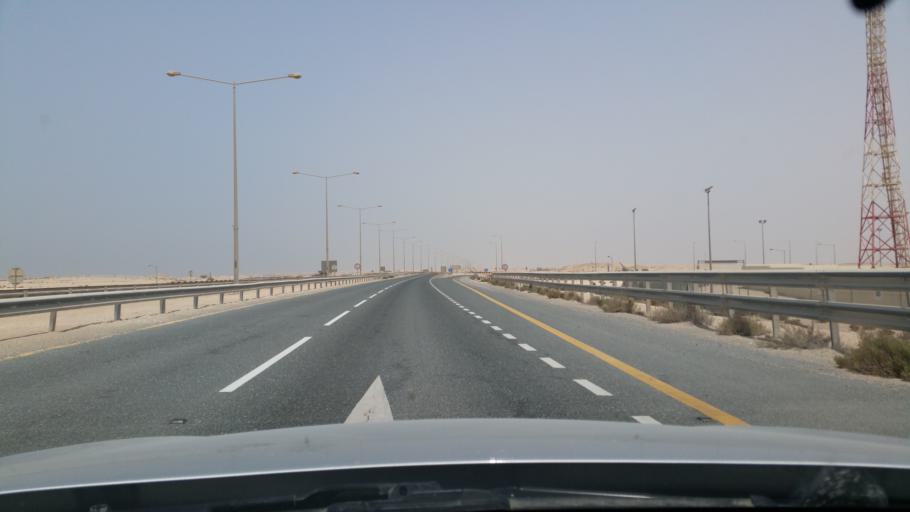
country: QA
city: Umm Bab
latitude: 25.2325
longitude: 50.8022
